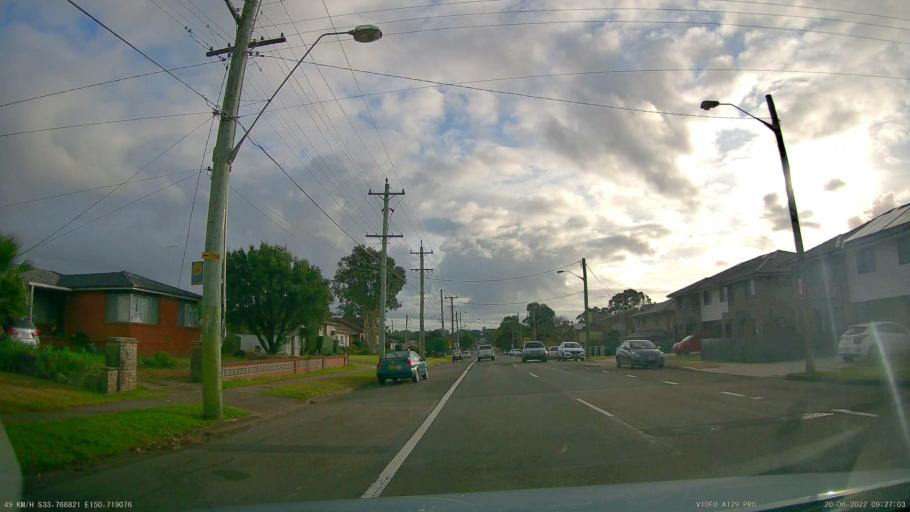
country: AU
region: New South Wales
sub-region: Penrith Municipality
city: Kingswood Park
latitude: -33.7666
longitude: 150.7191
